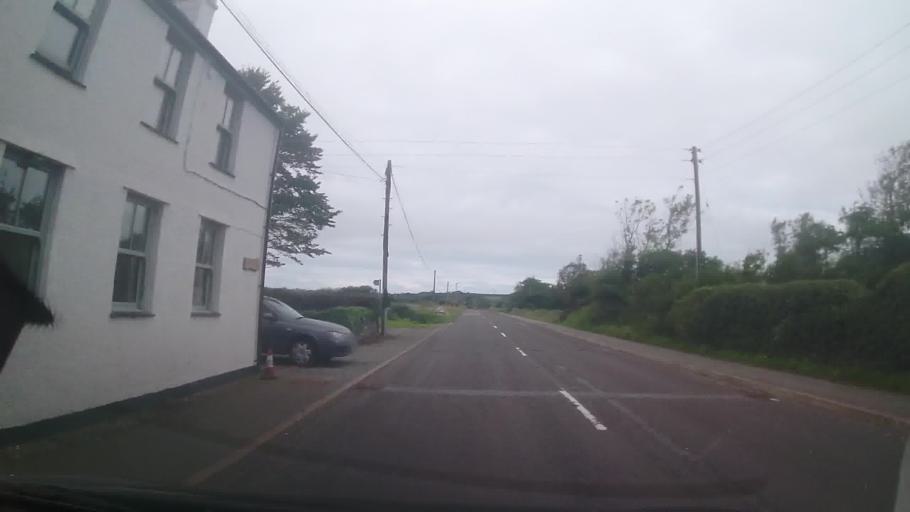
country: GB
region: Wales
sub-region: Gwynedd
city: Caernarfon
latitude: 53.1634
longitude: -4.3268
